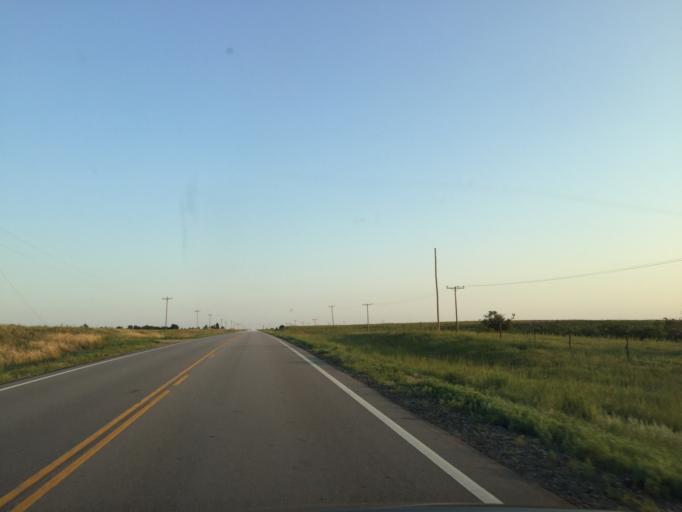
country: US
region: Kansas
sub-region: Ellsworth County
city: Ellsworth
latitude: 38.5731
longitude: -98.2018
